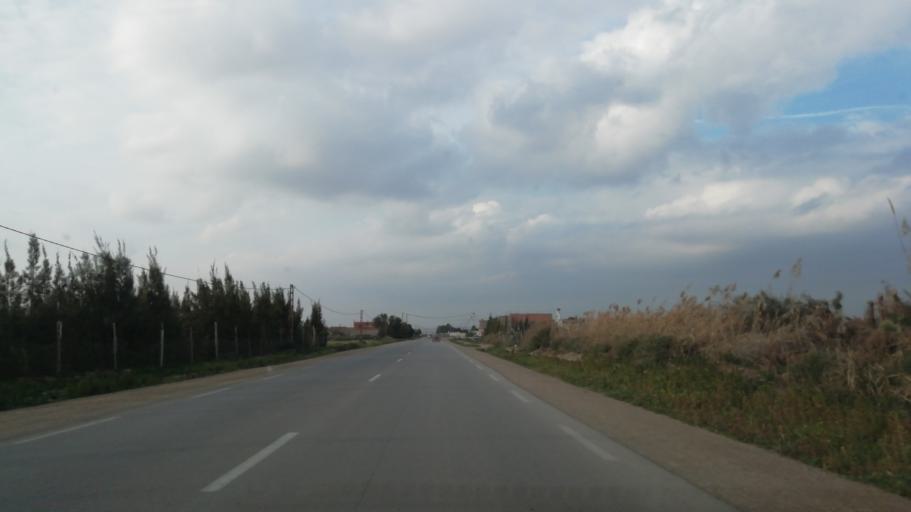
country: DZ
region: Mascara
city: Sig
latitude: 35.6883
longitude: -0.0161
